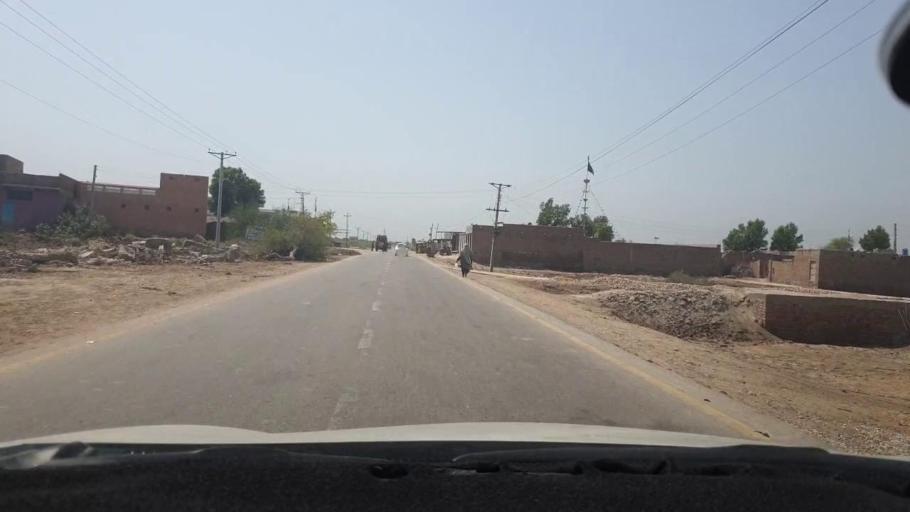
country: PK
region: Sindh
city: Shahdadpur
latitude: 25.8969
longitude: 68.5861
